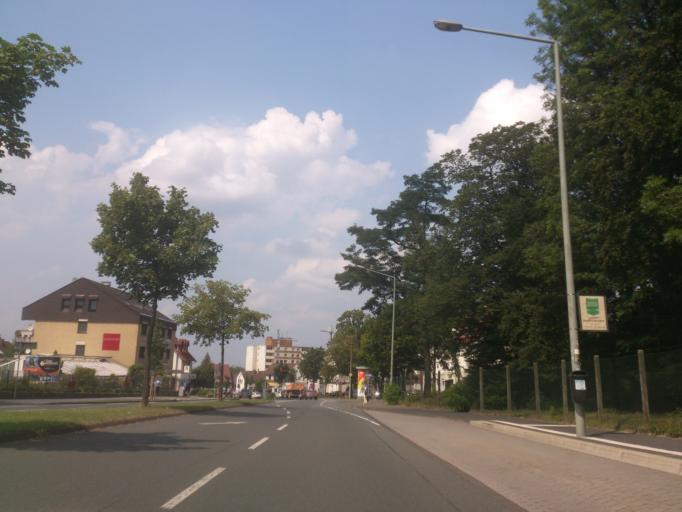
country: DE
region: North Rhine-Westphalia
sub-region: Regierungsbezirk Detmold
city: Paderborn
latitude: 51.7101
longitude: 8.7745
